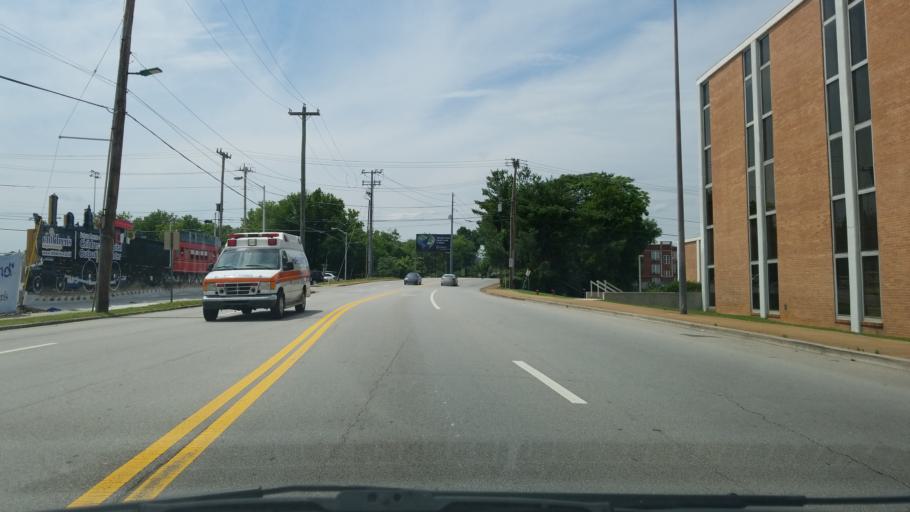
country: US
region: Tennessee
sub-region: Hamilton County
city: Chattanooga
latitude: 35.0485
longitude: -85.2923
